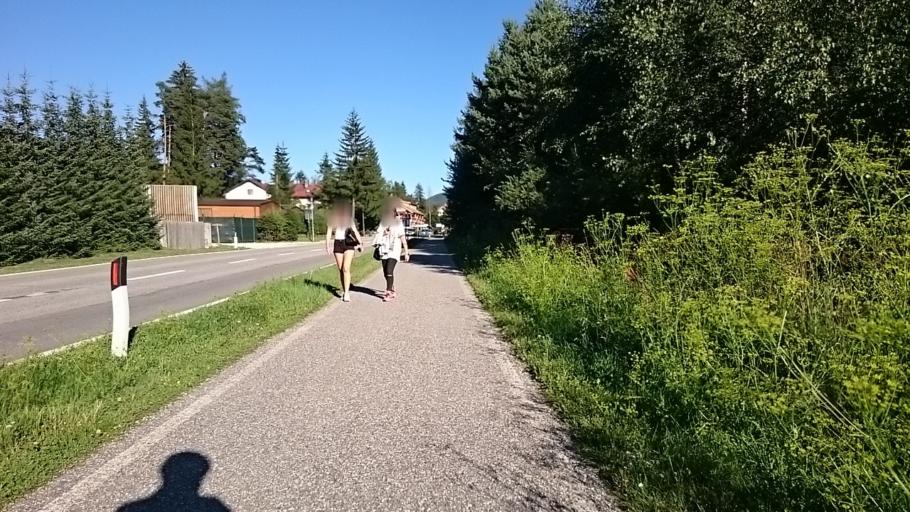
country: IT
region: Trentino-Alto Adige
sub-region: Bolzano
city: Villabassa
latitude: 46.7350
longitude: 12.1910
